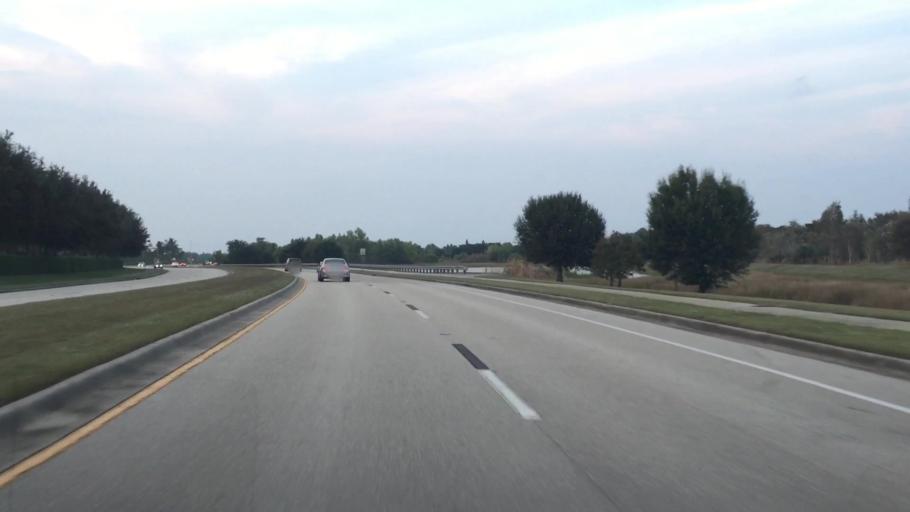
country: US
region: Florida
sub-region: Lee County
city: Estero
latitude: 26.4158
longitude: -81.8049
